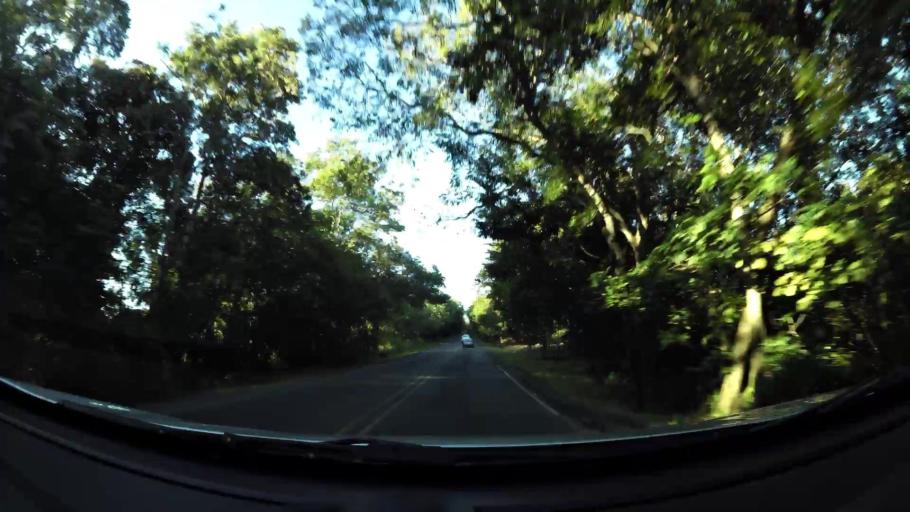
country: CR
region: Puntarenas
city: Miramar
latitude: 10.0980
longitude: -84.8131
